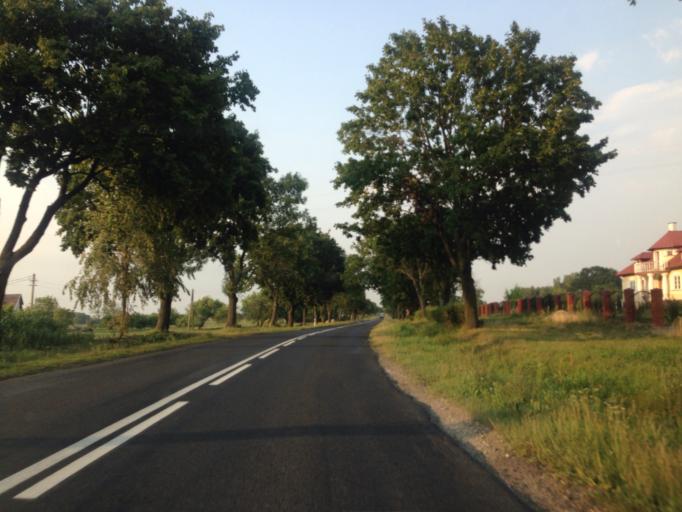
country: PL
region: Kujawsko-Pomorskie
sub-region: Powiat lipnowski
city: Chrostkowo
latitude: 52.9251
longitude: 19.2460
